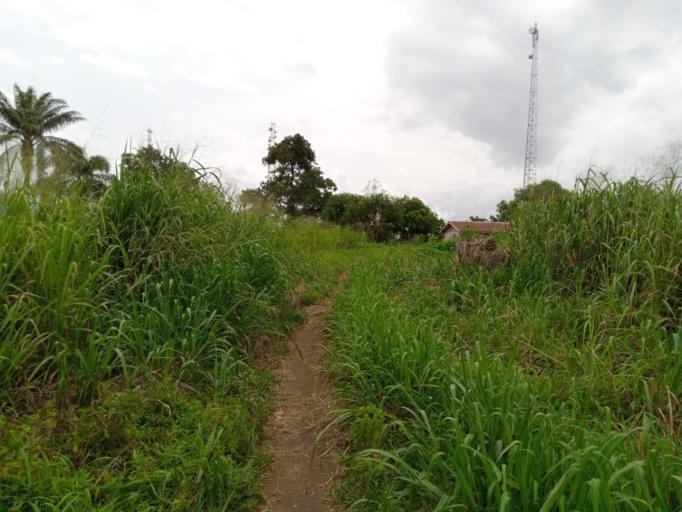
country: SL
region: Southern Province
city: Moyamba
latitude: 8.1644
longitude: -12.4231
